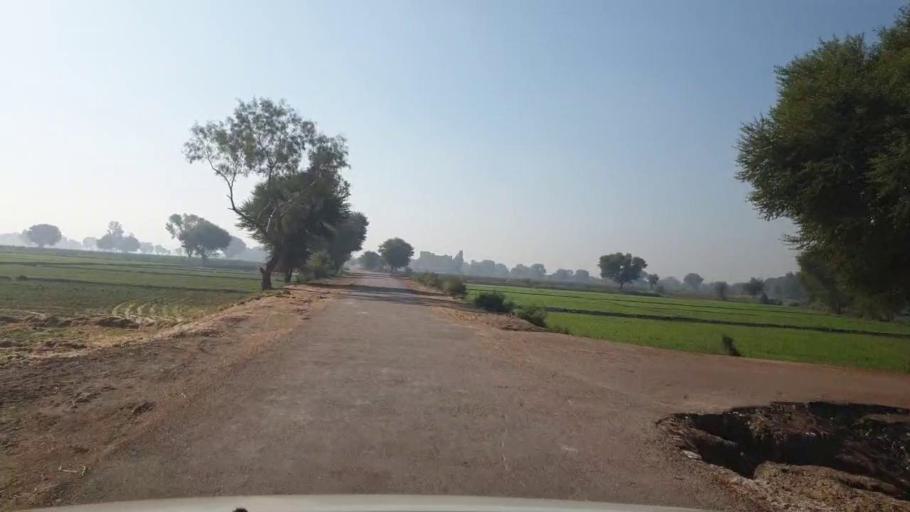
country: PK
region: Sindh
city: Dadu
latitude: 26.6537
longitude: 67.8225
